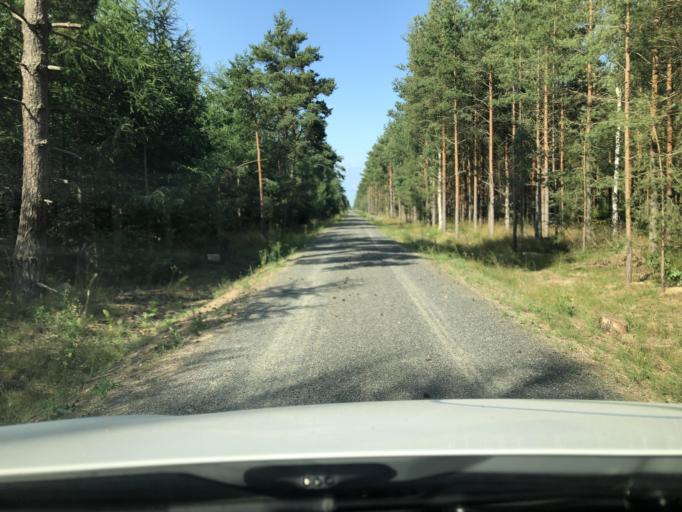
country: SE
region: Skane
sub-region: Kristianstads Kommun
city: Norra Asum
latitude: 55.9283
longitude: 14.1306
